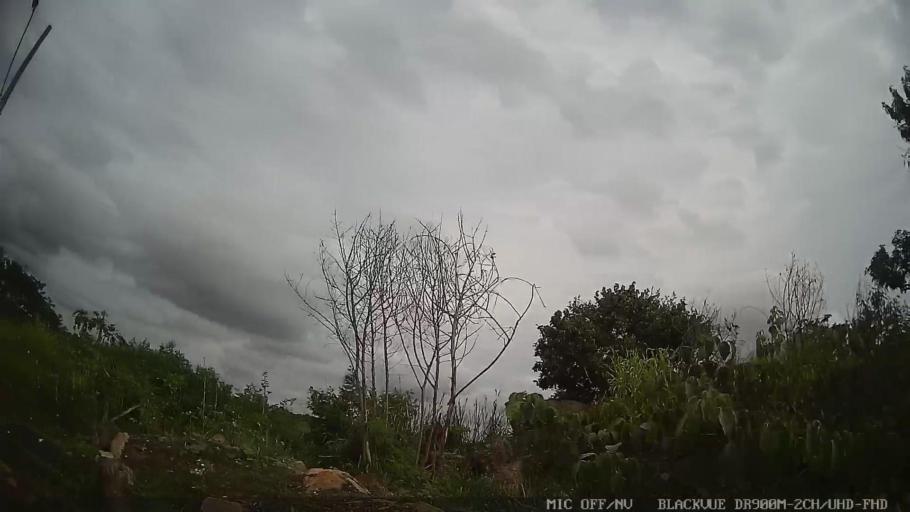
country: BR
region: Sao Paulo
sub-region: Salto
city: Salto
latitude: -23.2136
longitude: -47.2895
